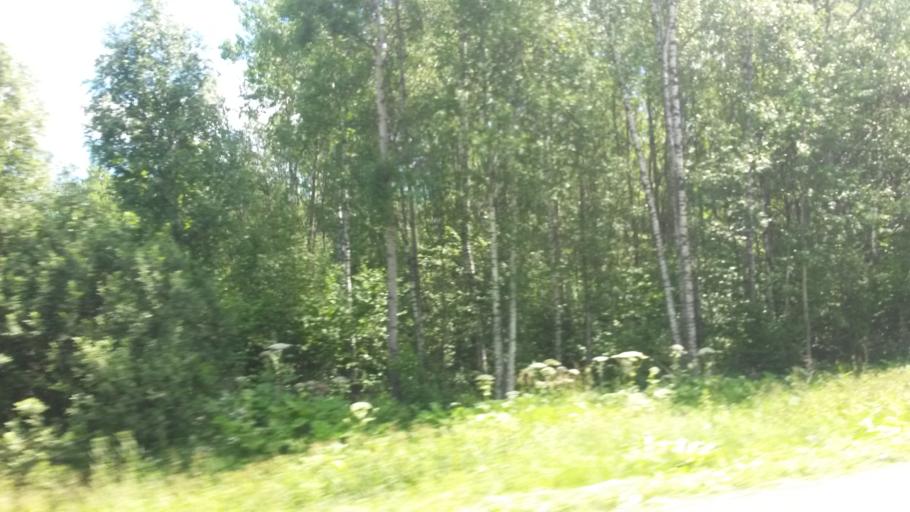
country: RU
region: Ivanovo
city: Rodniki
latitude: 57.1186
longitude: 41.7893
